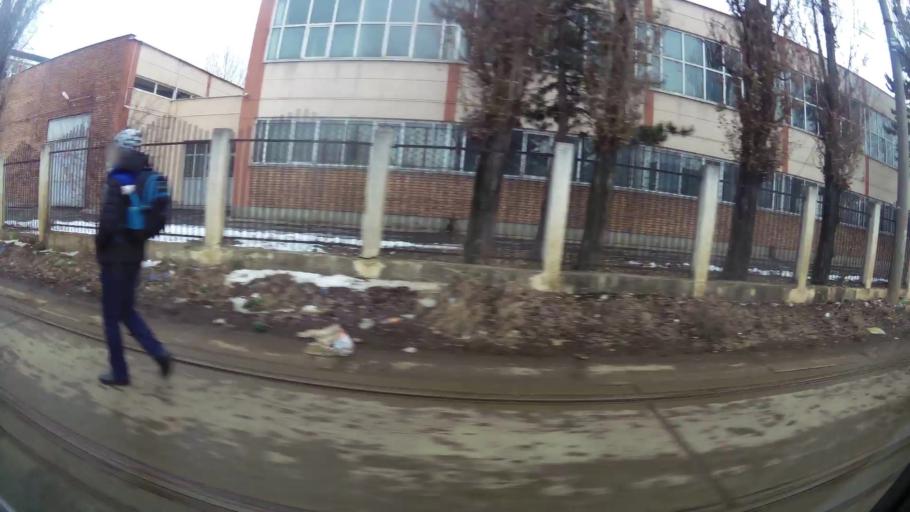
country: RO
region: Ilfov
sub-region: Comuna Glina
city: Catelu
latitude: 44.4051
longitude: 26.2031
